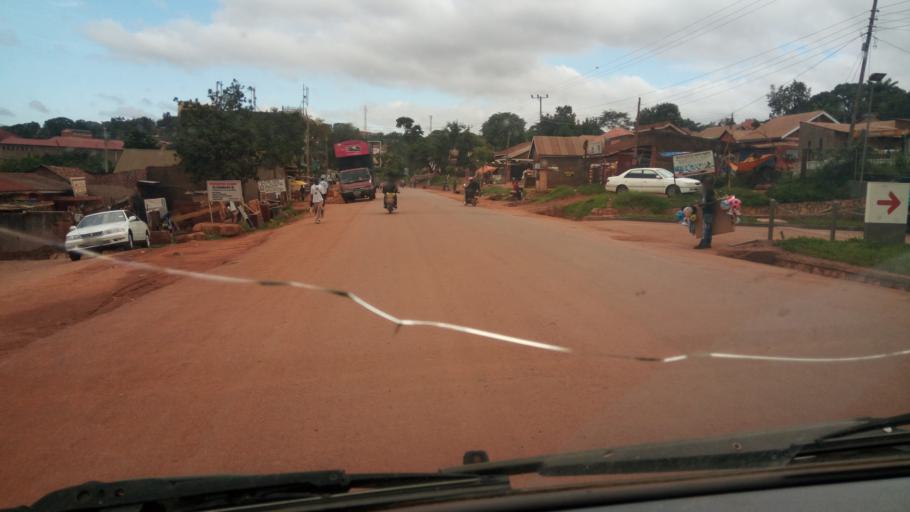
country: UG
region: Central Region
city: Kampala Central Division
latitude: 0.3356
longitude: 32.5485
